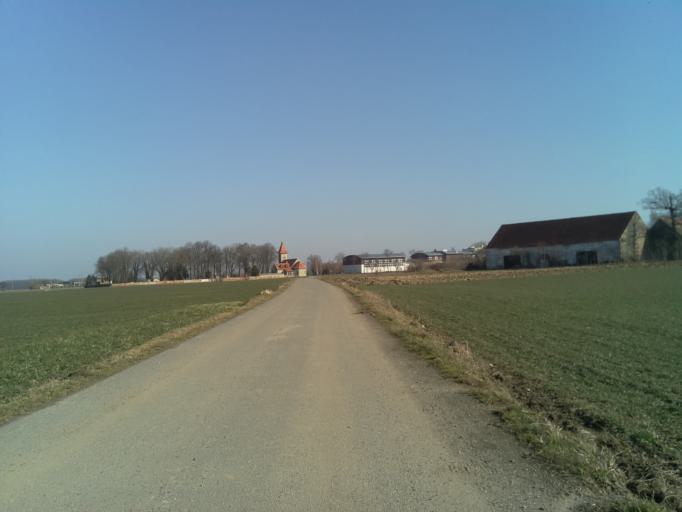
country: PL
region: Lower Silesian Voivodeship
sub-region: Powiat swidnicki
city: Swiebodzice
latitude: 50.8731
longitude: 16.3354
